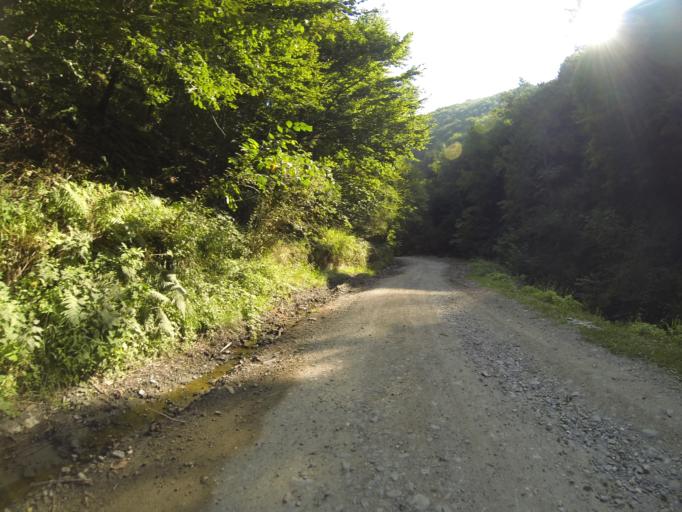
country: RO
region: Valcea
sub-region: Comuna Costesti
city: Bistrita
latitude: 45.2136
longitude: 24.0067
